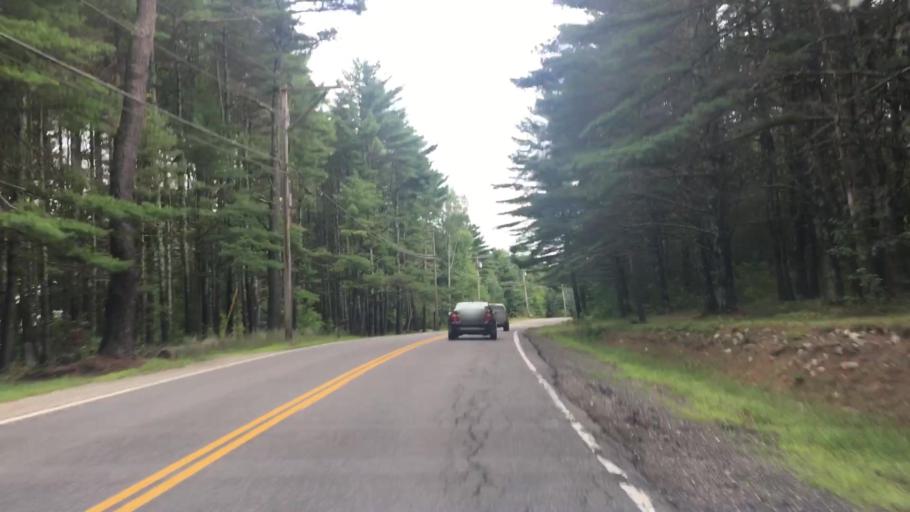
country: US
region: Maine
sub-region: York County
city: Lake Arrowhead
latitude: 43.6149
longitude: -70.7207
